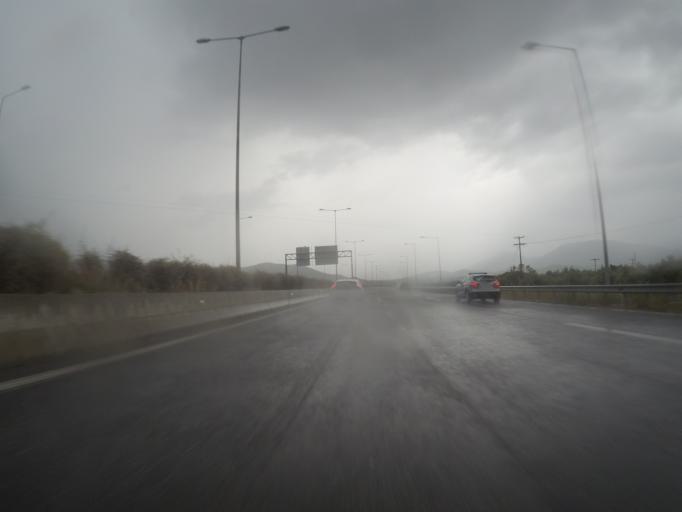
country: GR
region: Peloponnese
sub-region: Nomos Messinias
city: Meligalas
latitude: 37.2474
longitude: 22.0216
